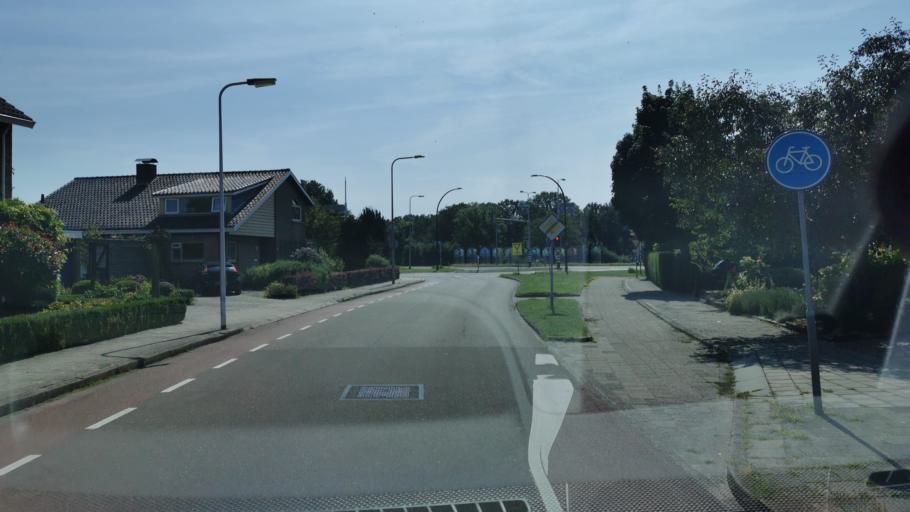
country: NL
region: Overijssel
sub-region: Gemeente Haaksbergen
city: Haaksbergen
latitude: 52.1515
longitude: 6.7289
